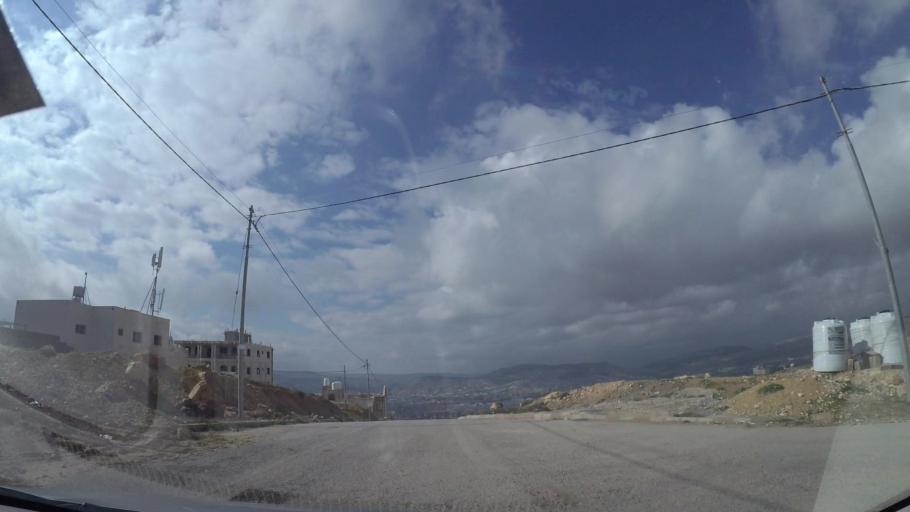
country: JO
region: Amman
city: Al Jubayhah
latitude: 32.0580
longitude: 35.8624
